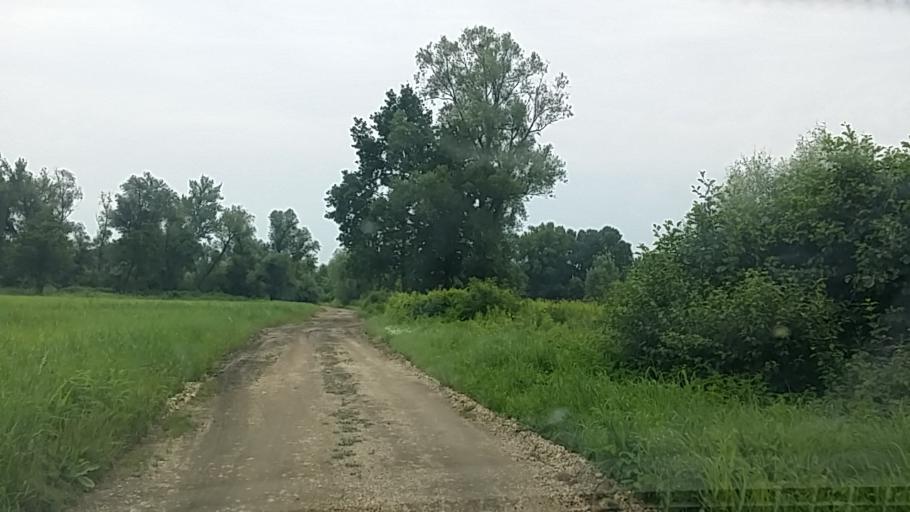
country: HR
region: Medimurska
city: Domasinec
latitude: 46.4682
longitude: 16.6405
